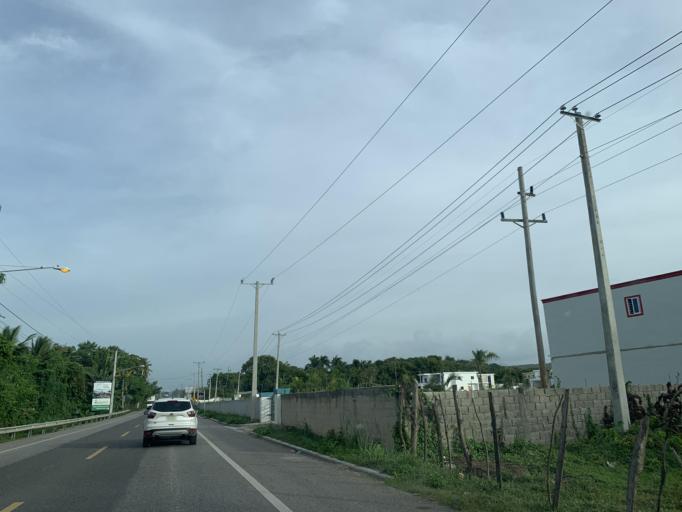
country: DO
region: Puerto Plata
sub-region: Puerto Plata
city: Puerto Plata
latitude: 19.7512
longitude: -70.6404
